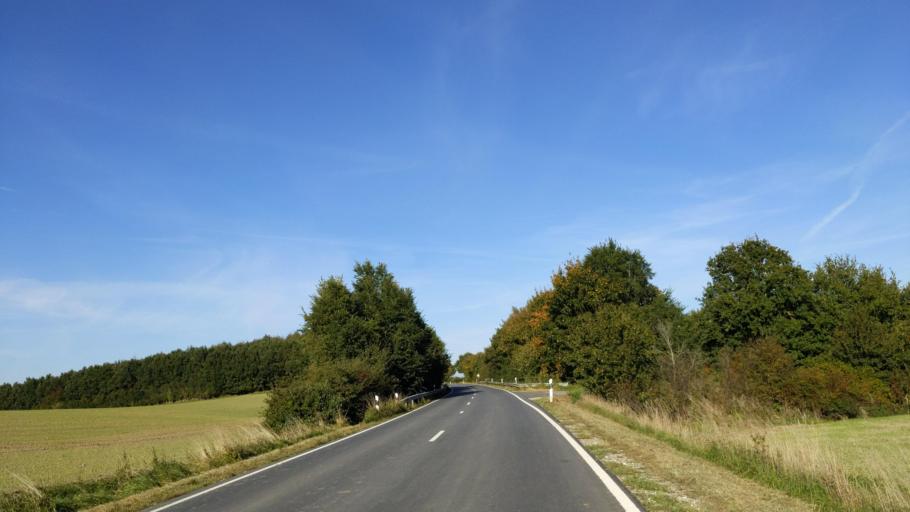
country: DE
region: Schleswig-Holstein
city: Ahrensbok
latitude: 54.0696
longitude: 10.5903
